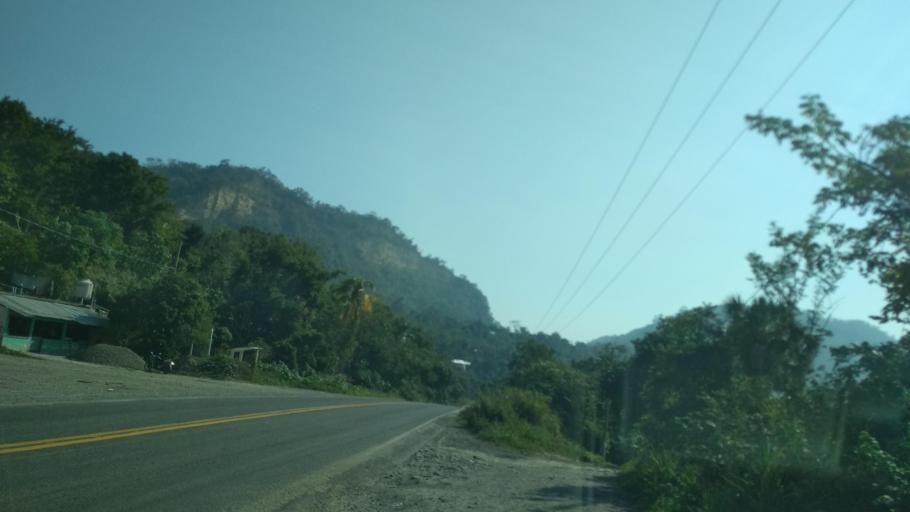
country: MX
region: Veracruz
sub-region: Papantla
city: Polutla
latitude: 20.4642
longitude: -97.1958
